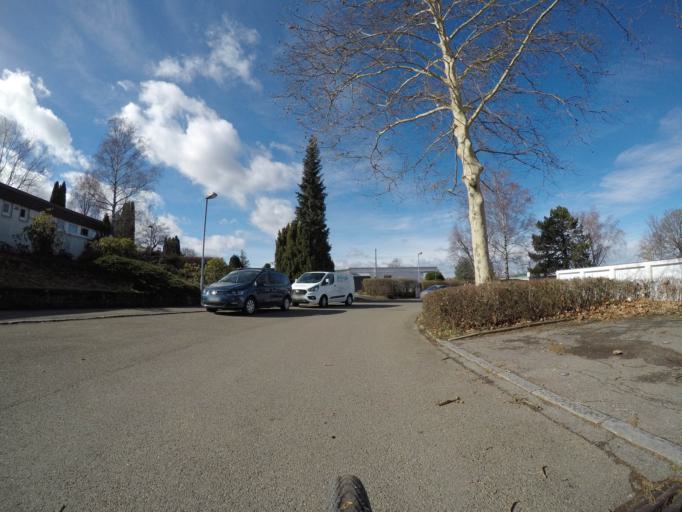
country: DE
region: Baden-Wuerttemberg
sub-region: Tuebingen Region
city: Reutlingen
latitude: 48.5179
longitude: 9.2135
